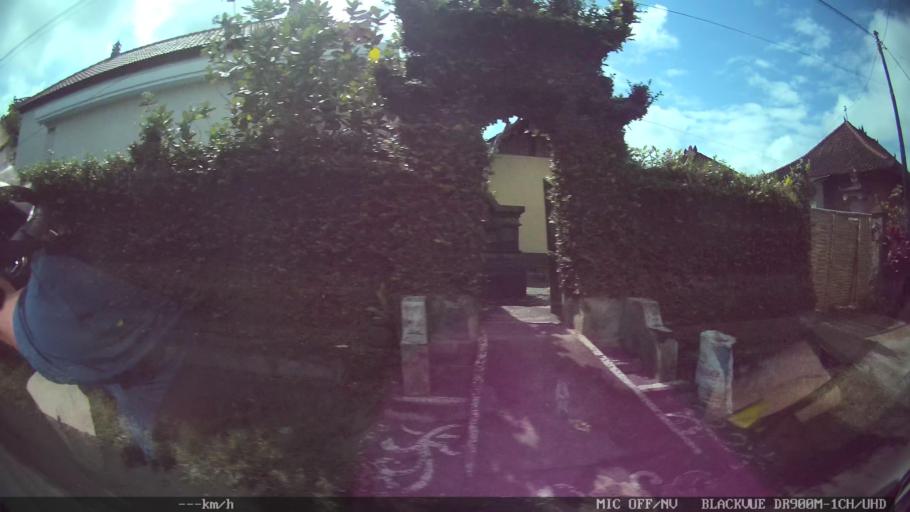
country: ID
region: Bali
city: Banjar Tebongkang
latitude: -8.5340
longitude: 115.2523
